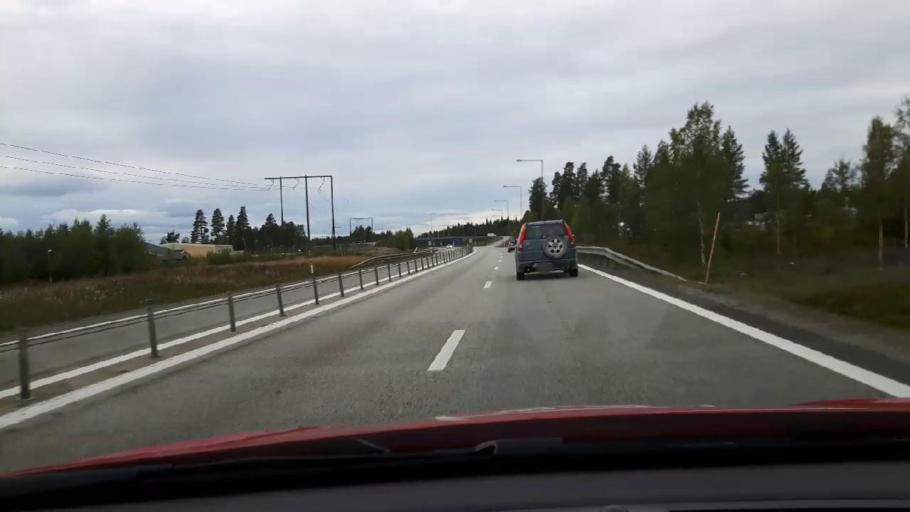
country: SE
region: Jaemtland
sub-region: OEstersunds Kommun
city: Brunflo
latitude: 63.1612
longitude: 14.7518
